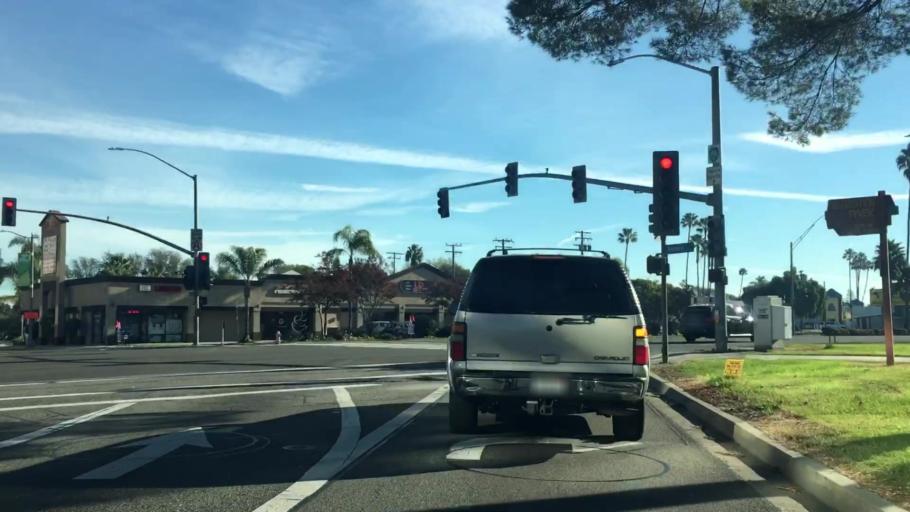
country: US
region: California
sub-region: Los Angeles County
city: Signal Hill
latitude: 33.7825
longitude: -118.1329
